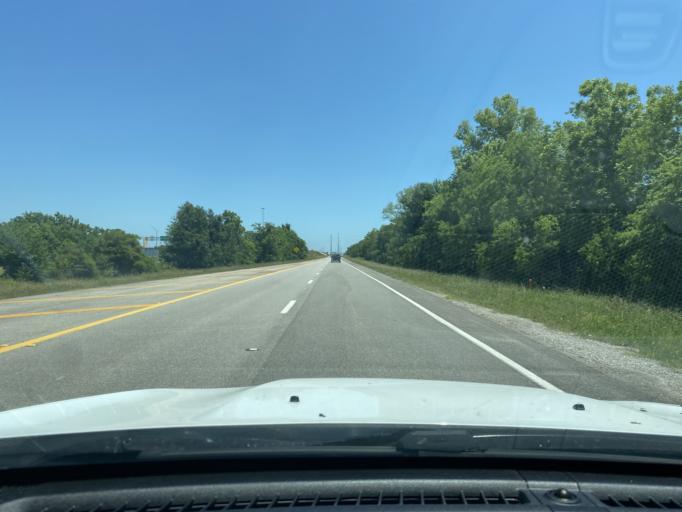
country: US
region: Texas
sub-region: Waller County
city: Waller
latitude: 30.0251
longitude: -95.8399
